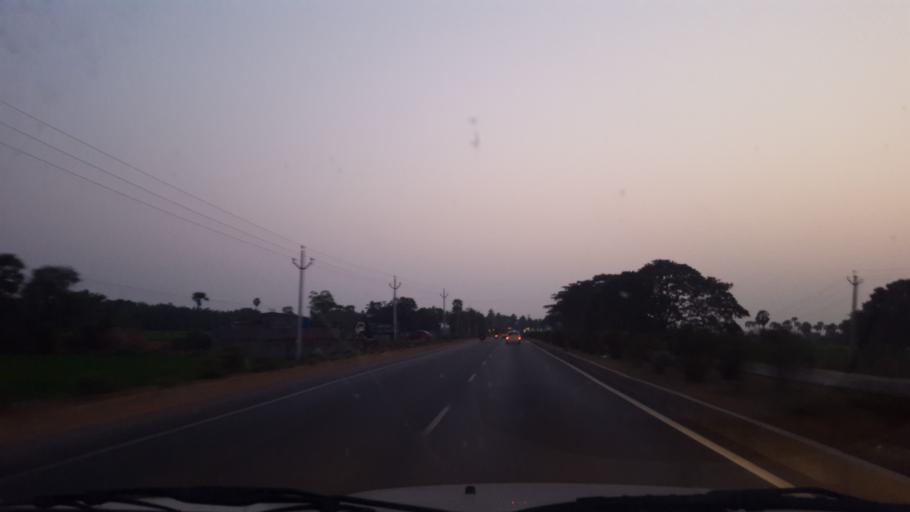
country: IN
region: Andhra Pradesh
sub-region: East Godavari
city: Peddapuram
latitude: 17.1518
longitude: 81.9871
